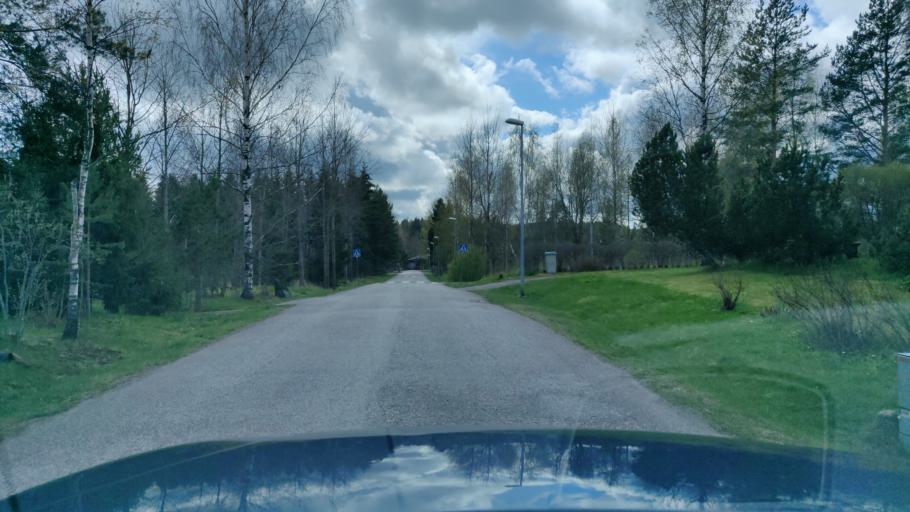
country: FI
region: Uusimaa
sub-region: Helsinki
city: Nurmijaervi
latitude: 60.3639
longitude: 24.7423
